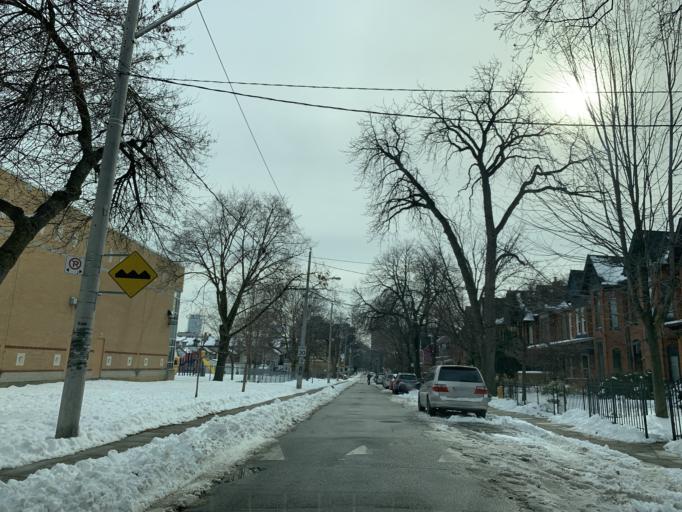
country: CA
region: Ontario
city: Toronto
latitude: 43.6608
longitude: -79.3680
